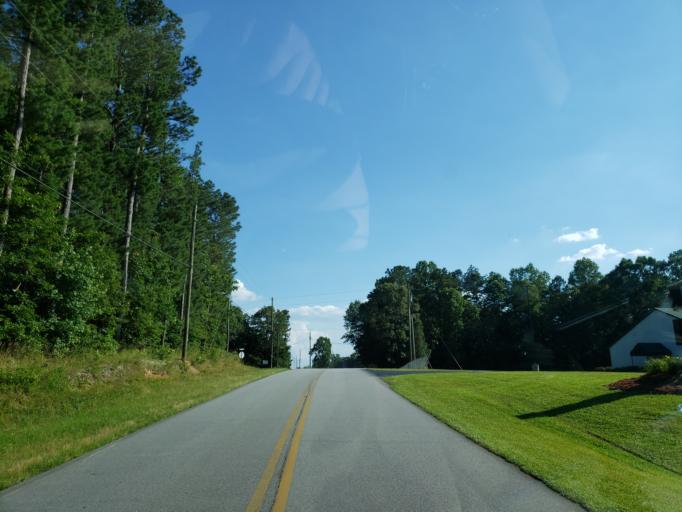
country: US
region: Georgia
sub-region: Carroll County
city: Carrollton
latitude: 33.6595
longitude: -85.0861
